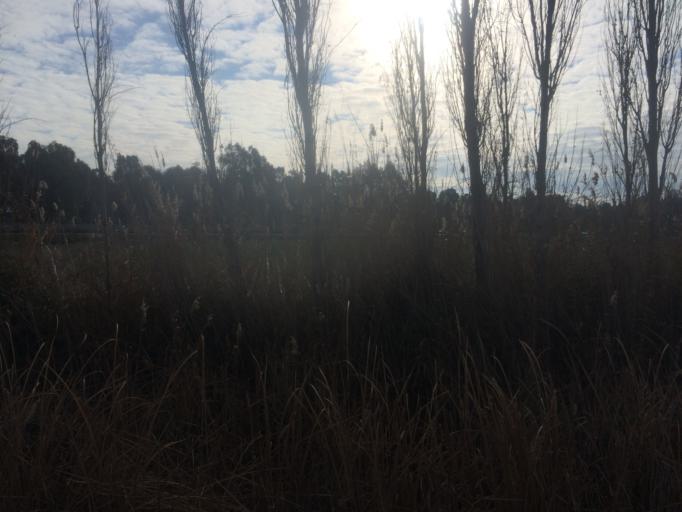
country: TR
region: Izmir
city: Karsiyaka
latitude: 38.4935
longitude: 26.9592
